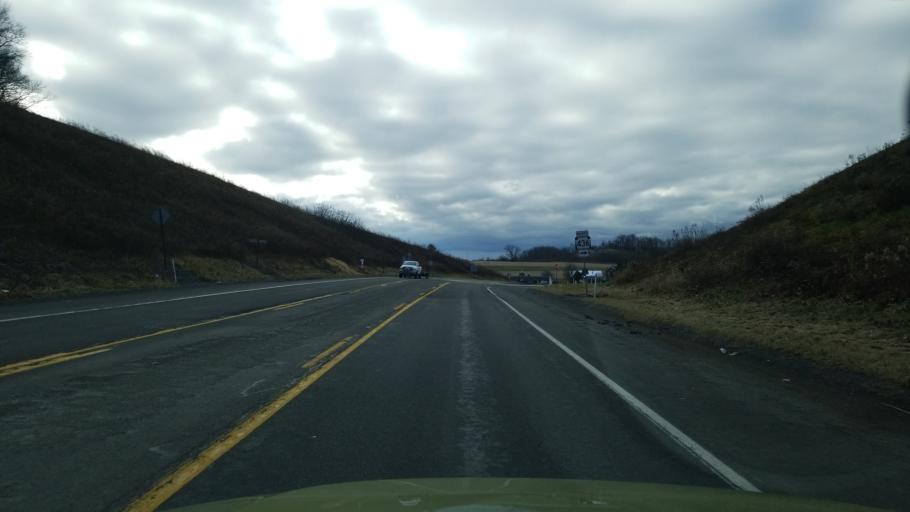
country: US
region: Pennsylvania
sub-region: Jefferson County
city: Punxsutawney
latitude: 40.9196
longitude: -78.9862
